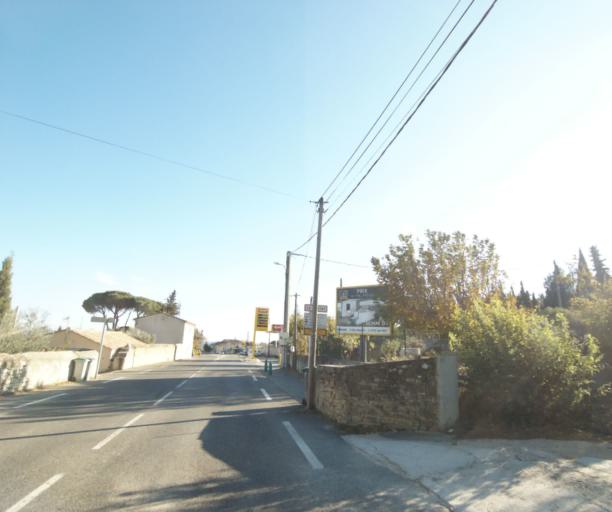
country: FR
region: Provence-Alpes-Cote d'Azur
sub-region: Departement des Bouches-du-Rhone
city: La Ciotat
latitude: 43.1937
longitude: 5.6002
